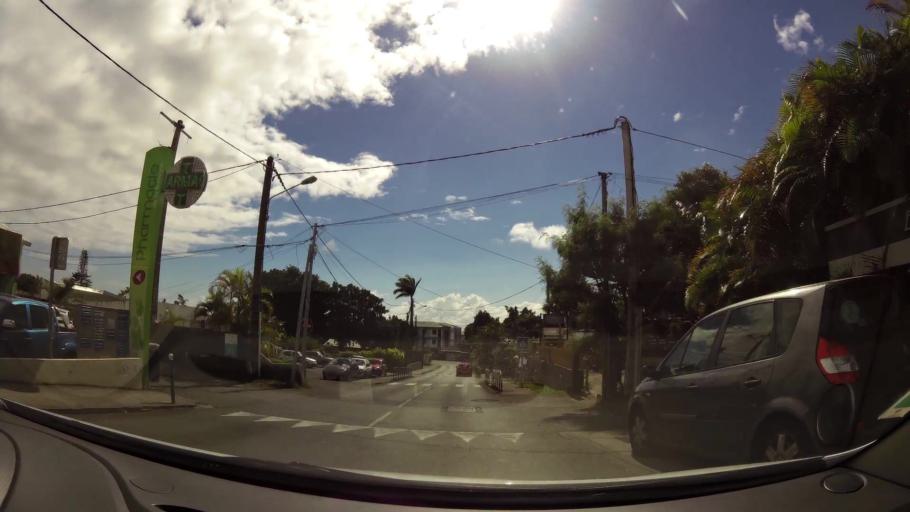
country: RE
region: Reunion
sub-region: Reunion
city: Saint-Denis
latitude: -20.9185
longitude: 55.4942
